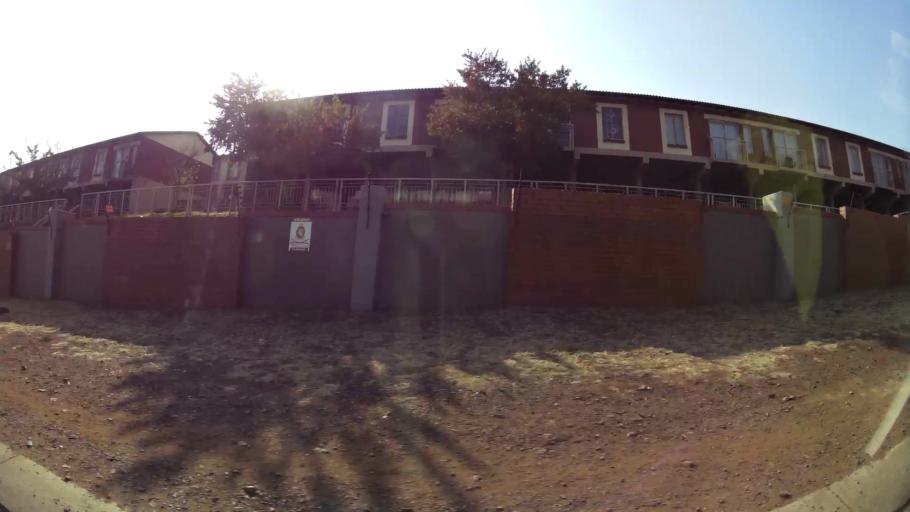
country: ZA
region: Gauteng
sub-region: City of Tshwane Metropolitan Municipality
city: Pretoria
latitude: -25.7664
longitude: 28.3474
